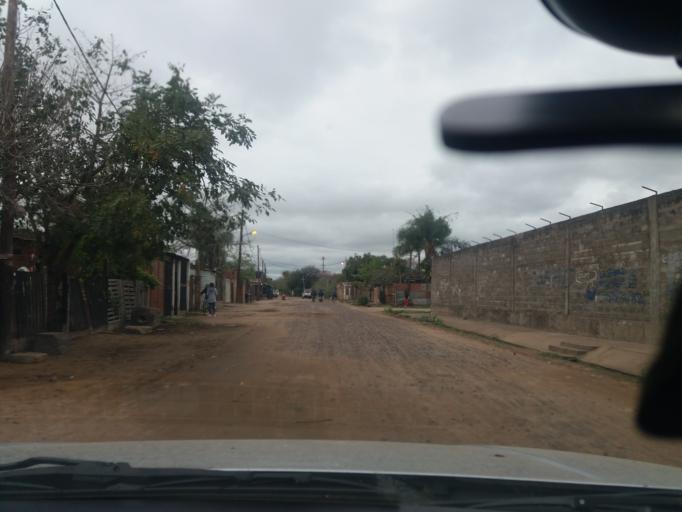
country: AR
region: Corrientes
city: Corrientes
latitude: -27.5124
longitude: -58.8297
